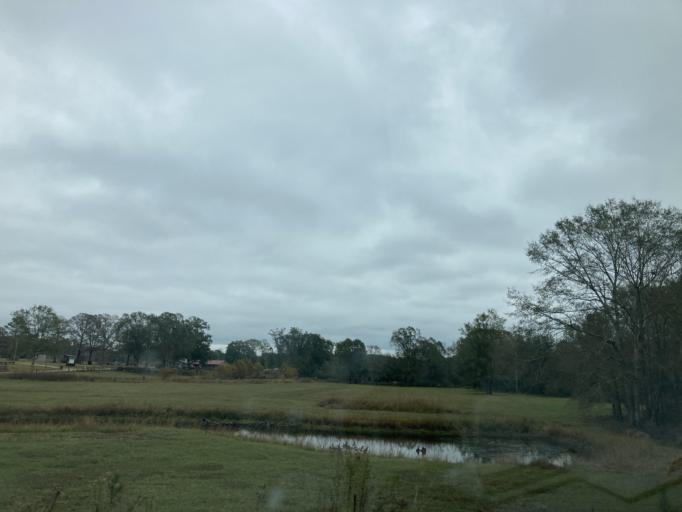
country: US
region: Mississippi
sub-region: Lamar County
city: Purvis
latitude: 31.2453
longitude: -89.4962
